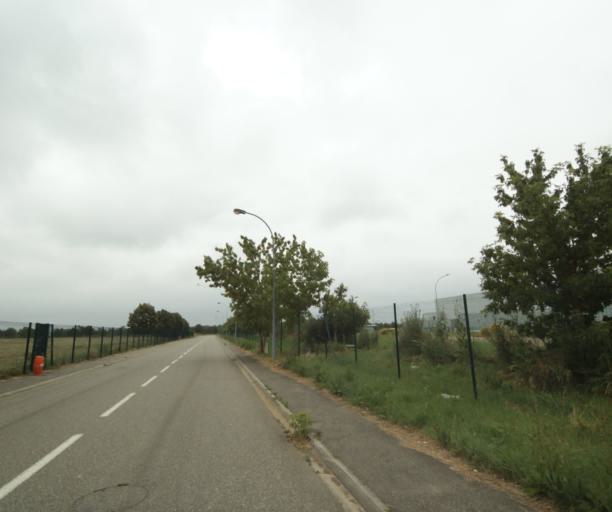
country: FR
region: Midi-Pyrenees
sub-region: Departement du Tarn-et-Garonne
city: Bressols
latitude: 43.9765
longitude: 1.3225
